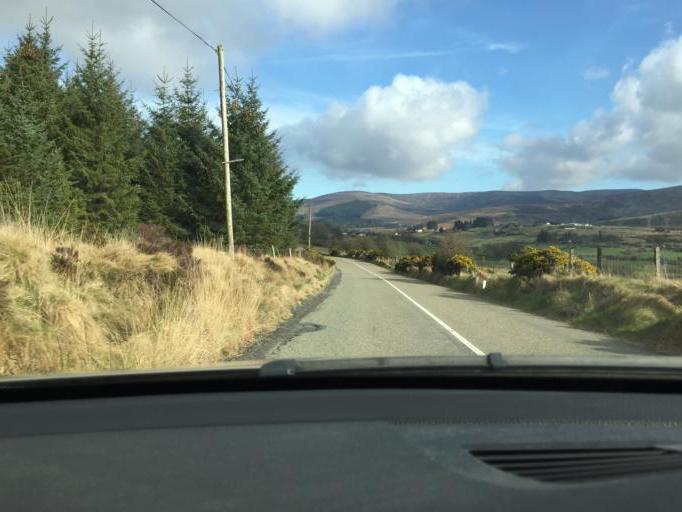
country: IE
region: Leinster
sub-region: Wicklow
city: Valleymount
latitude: 53.0628
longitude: -6.5127
